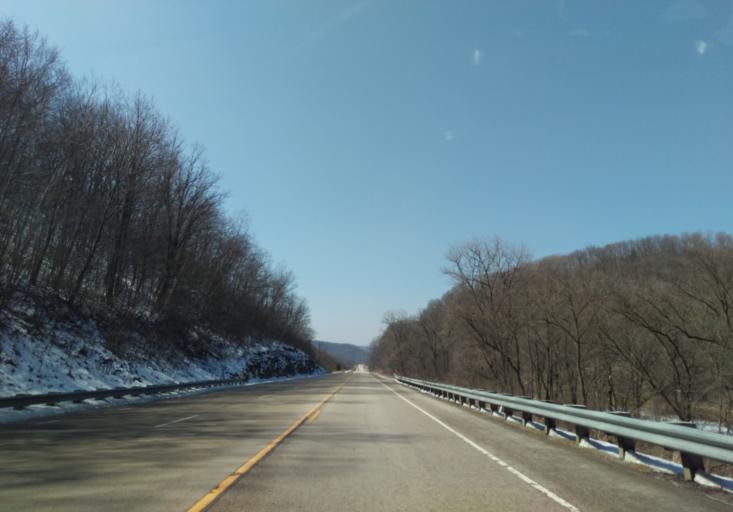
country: US
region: Wisconsin
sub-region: Vernon County
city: Viroqua
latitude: 43.4497
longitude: -90.7165
